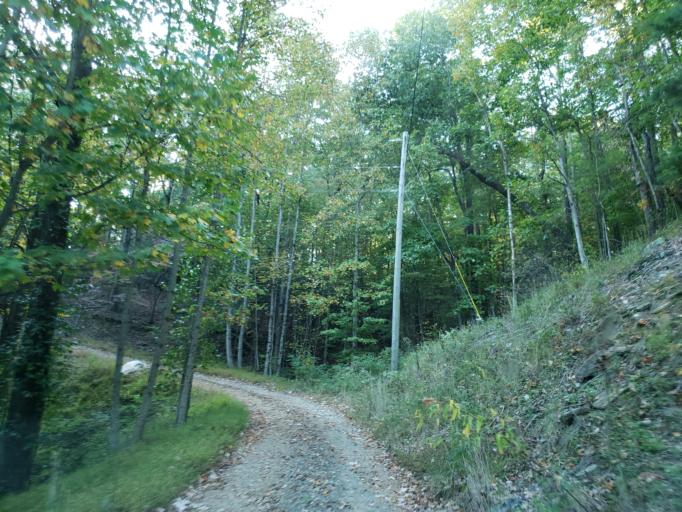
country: US
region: Georgia
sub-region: Fannin County
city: Blue Ridge
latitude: 34.6592
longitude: -84.2577
